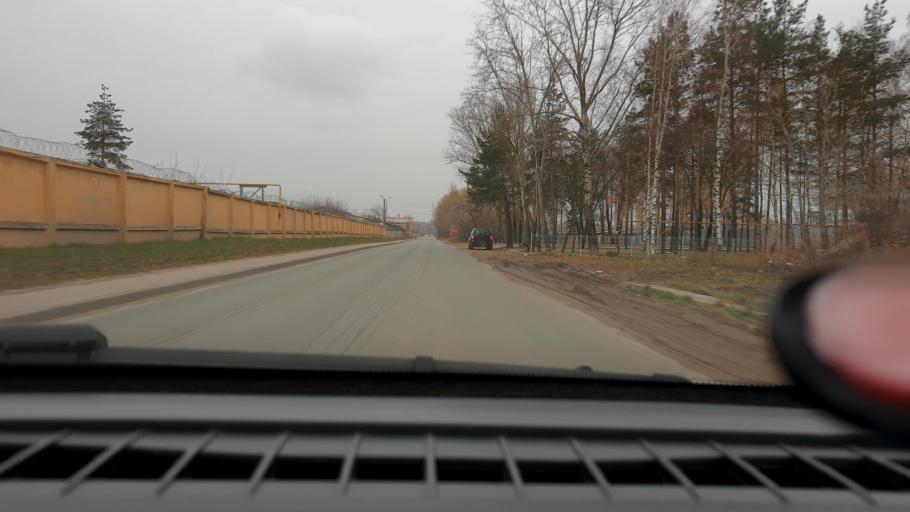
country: RU
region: Nizjnij Novgorod
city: Gorbatovka
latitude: 56.3382
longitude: 43.8066
